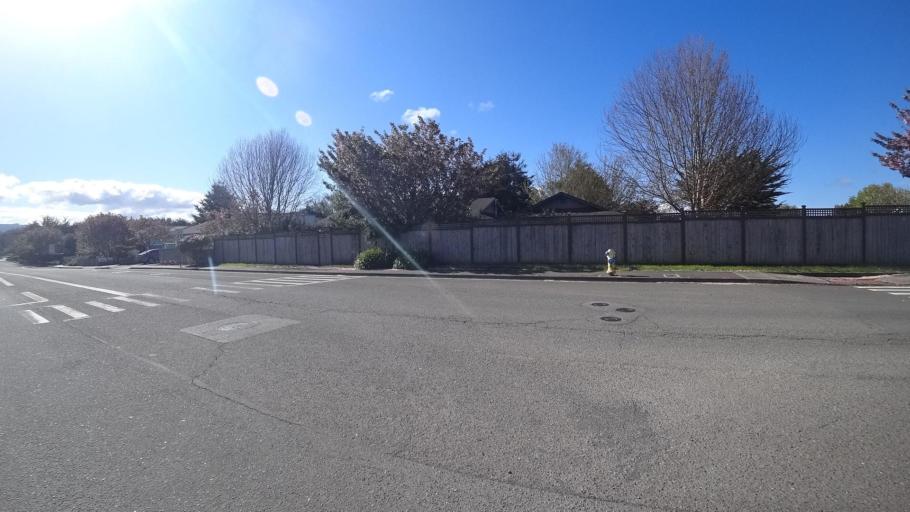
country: US
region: California
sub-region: Humboldt County
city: McKinleyville
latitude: 40.9343
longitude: -124.1066
